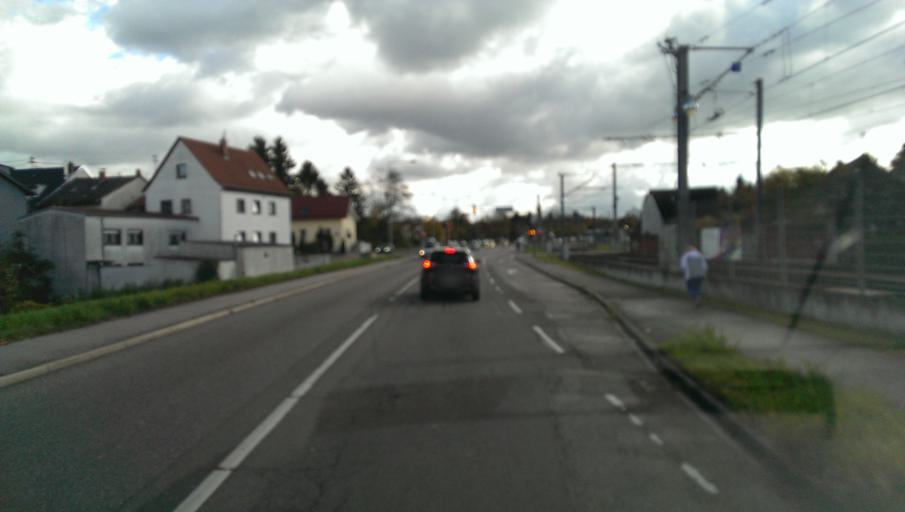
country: DE
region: Baden-Wuerttemberg
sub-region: Karlsruhe Region
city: Rheinstetten
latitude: 49.0362
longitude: 8.3345
